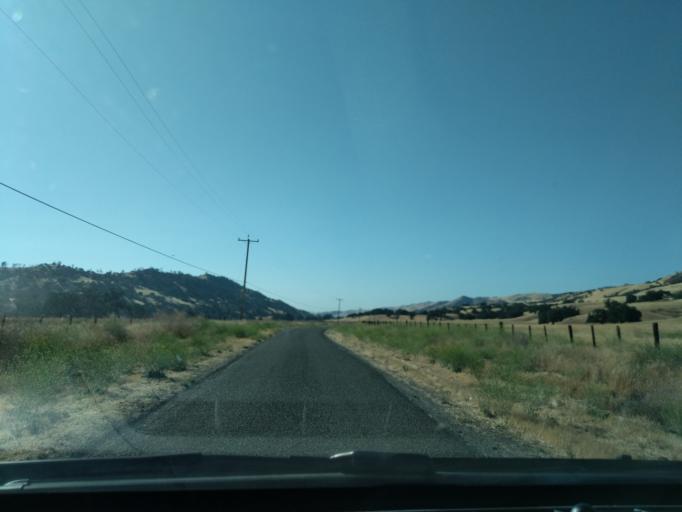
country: US
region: California
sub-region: San Luis Obispo County
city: San Miguel
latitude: 36.1208
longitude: -120.7333
